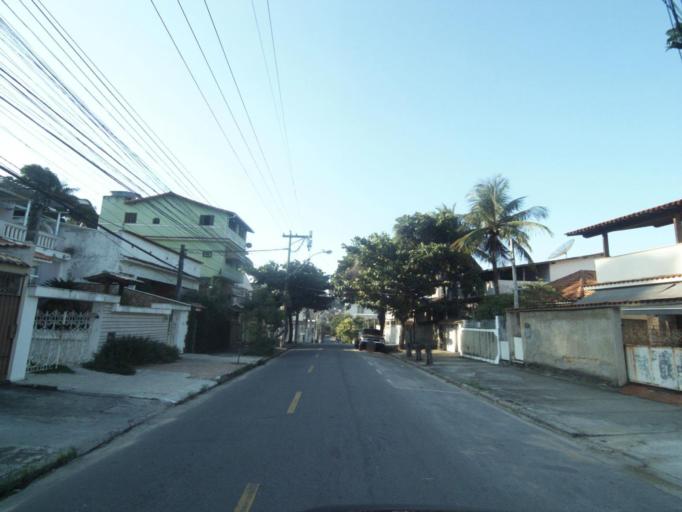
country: BR
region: Rio de Janeiro
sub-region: Niteroi
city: Niteroi
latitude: -22.8853
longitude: -43.0940
